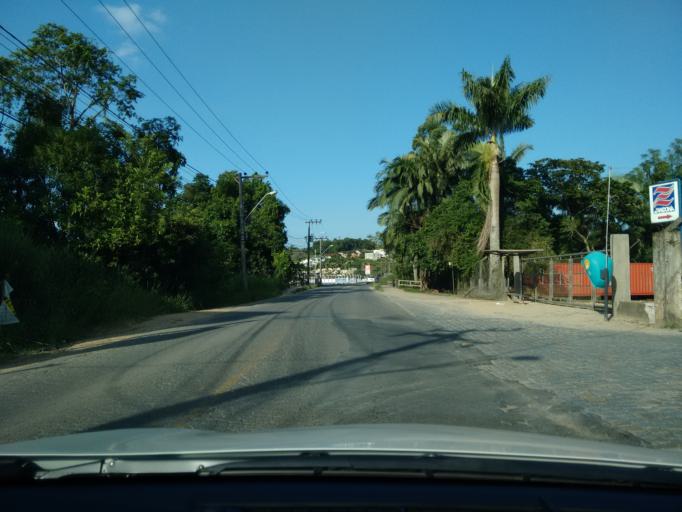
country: BR
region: Santa Catarina
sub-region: Blumenau
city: Blumenau
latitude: -26.8510
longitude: -49.0870
